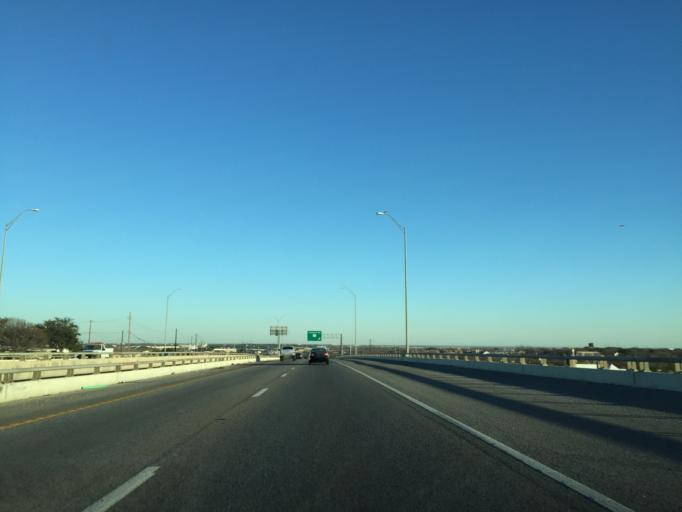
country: US
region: Texas
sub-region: Travis County
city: Austin
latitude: 30.3386
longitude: -97.6993
